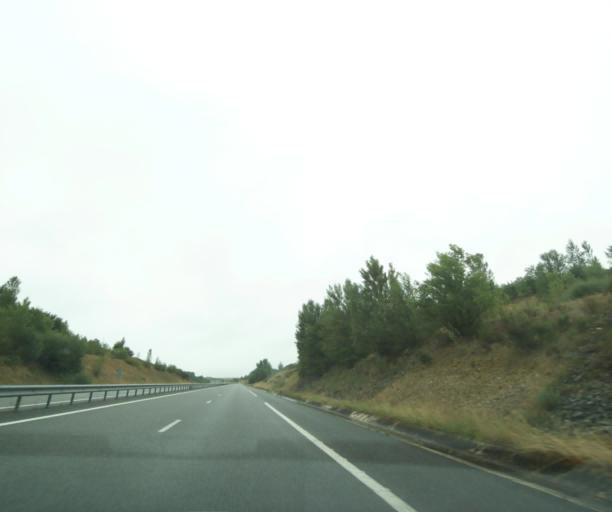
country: FR
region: Midi-Pyrenees
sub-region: Departement du Tarn
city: Carmaux
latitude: 44.0483
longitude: 2.2113
